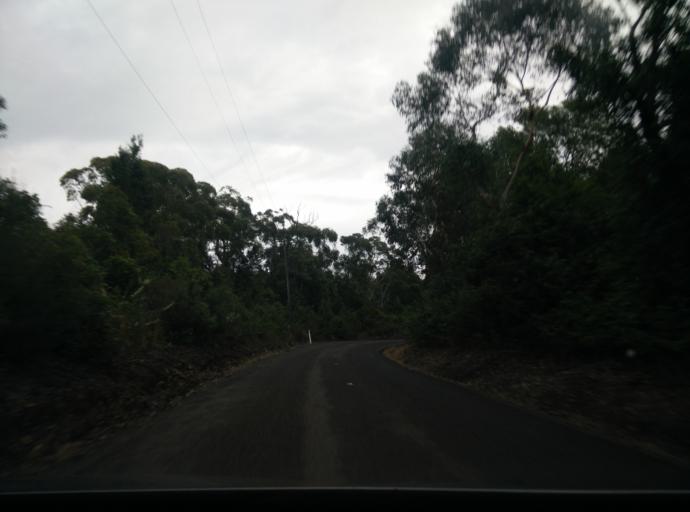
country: AU
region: New South Wales
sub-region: Gosford Shire
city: Narara
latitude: -33.3510
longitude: 151.2928
